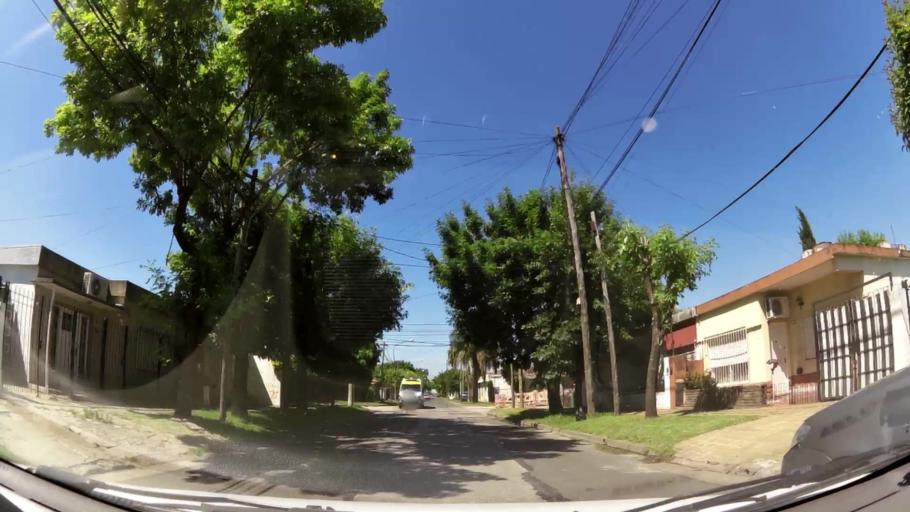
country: AR
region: Buenos Aires
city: Ituzaingo
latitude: -34.6660
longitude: -58.6599
